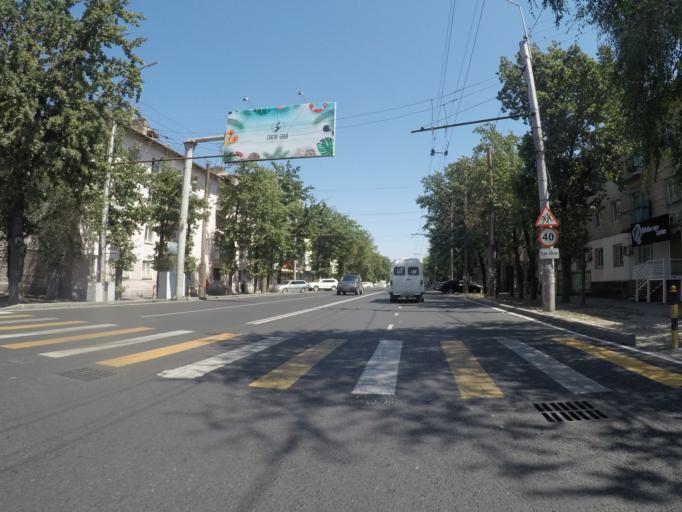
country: KG
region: Chuy
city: Bishkek
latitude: 42.8436
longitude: 74.5809
